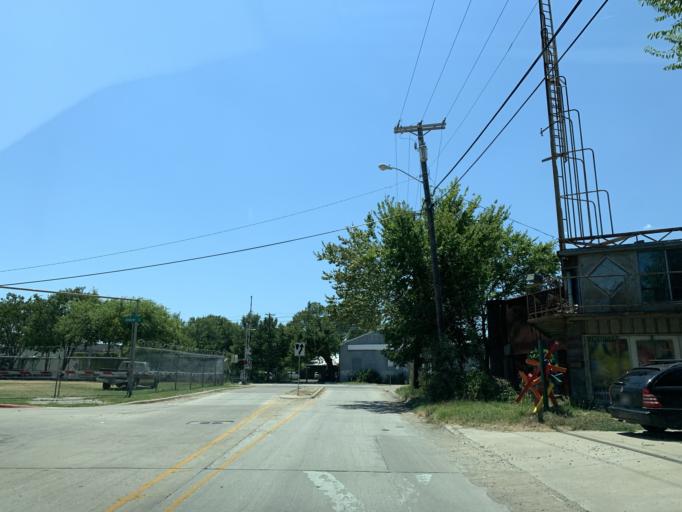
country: US
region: Texas
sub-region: Dallas County
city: Dallas
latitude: 32.7788
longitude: -96.7695
